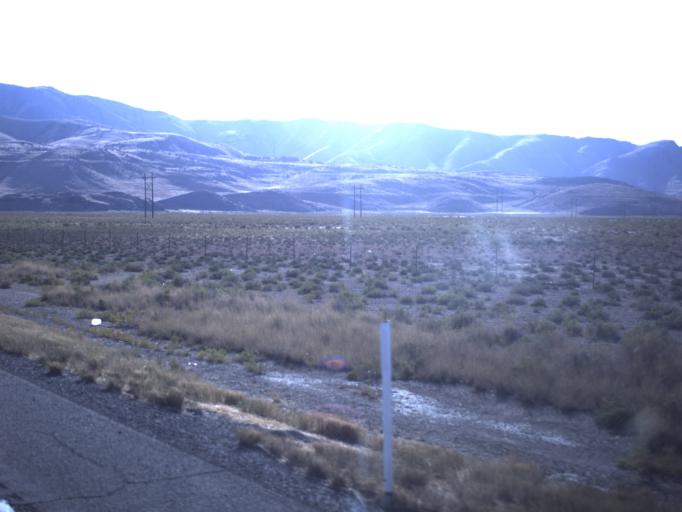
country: US
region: Utah
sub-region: Tooele County
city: Grantsville
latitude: 40.6944
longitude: -112.5328
